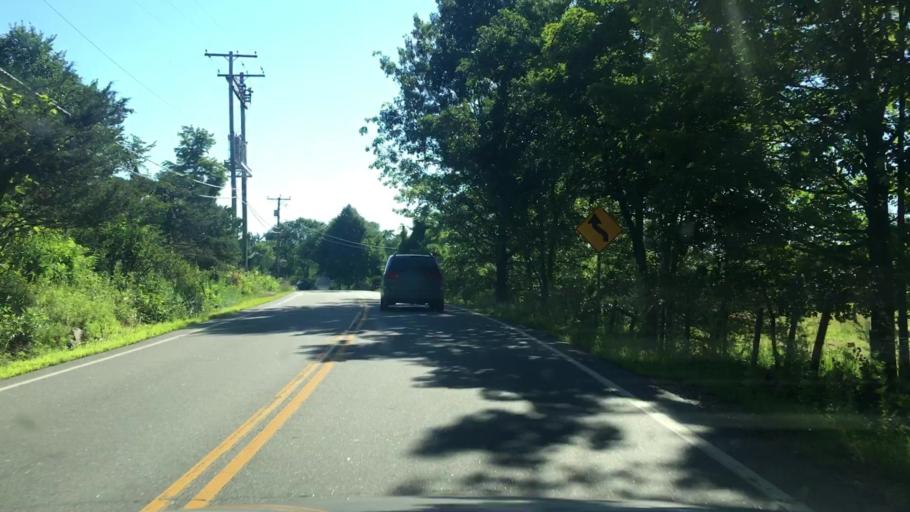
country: US
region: New Hampshire
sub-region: Rockingham County
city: Brentwood
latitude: 42.9923
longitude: -71.0235
